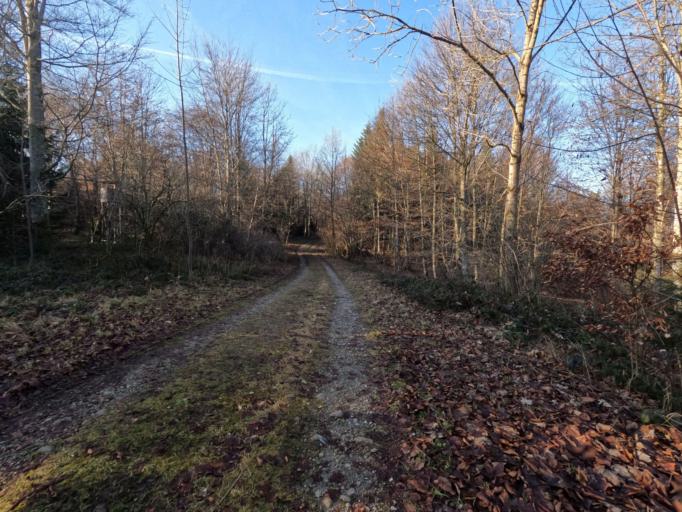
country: DE
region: Bavaria
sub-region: Upper Bavaria
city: Traunstein
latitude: 47.8952
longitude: 12.6280
